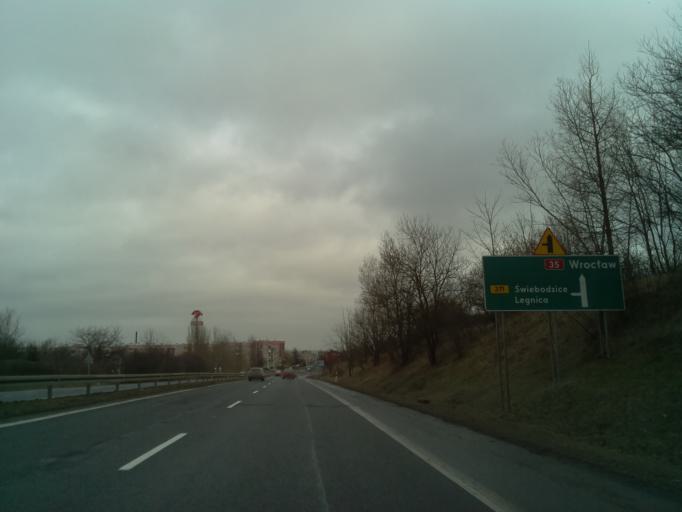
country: PL
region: Lower Silesian Voivodeship
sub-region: Powiat swidnicki
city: Swiebodzice
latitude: 50.8543
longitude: 16.3320
